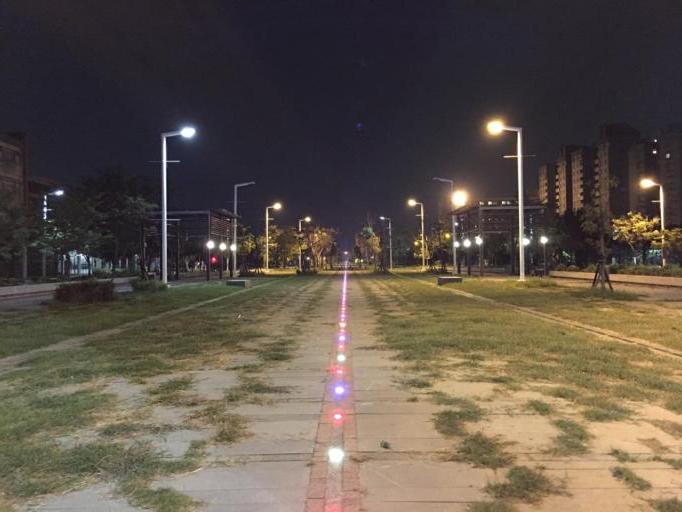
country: TW
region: Taiwan
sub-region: Chiayi
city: Taibao
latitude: 23.4678
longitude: 120.2940
